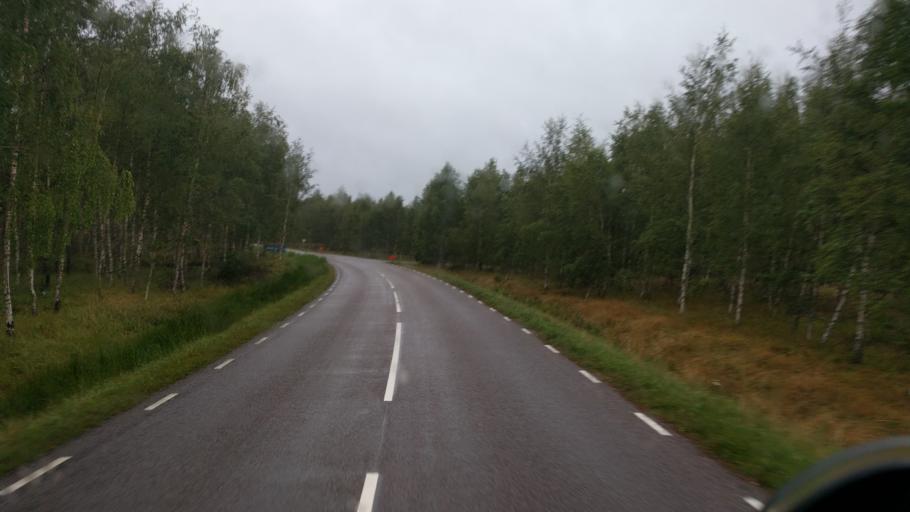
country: SE
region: Kalmar
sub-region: Vasterviks Kommun
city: Ankarsrum
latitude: 57.7960
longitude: 16.3646
